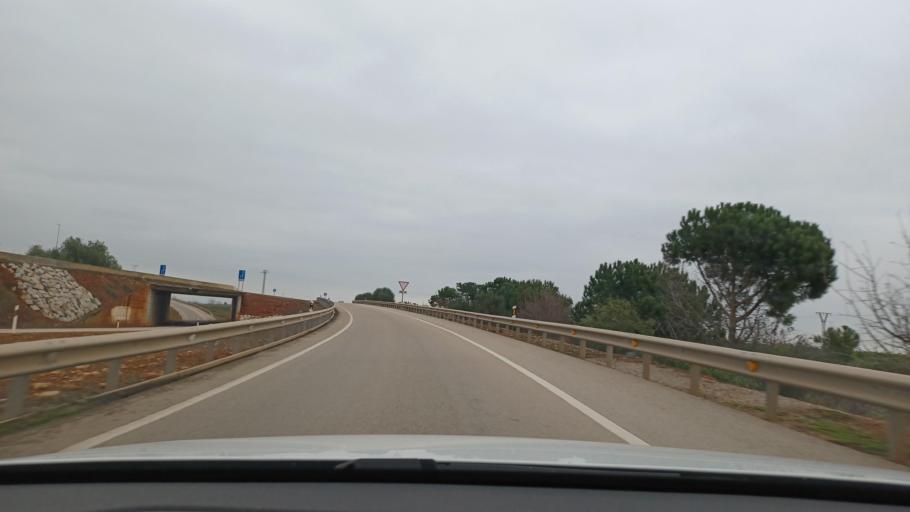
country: ES
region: Valencia
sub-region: Provincia de Castello
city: Nules
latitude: 39.8588
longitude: -0.1682
